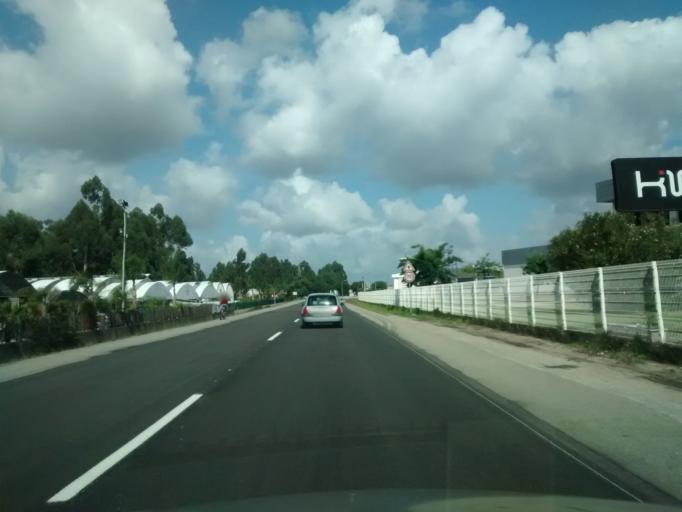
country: PT
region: Aveiro
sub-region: Oliveira do Bairro
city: Oia
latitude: 40.5383
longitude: -8.5266
